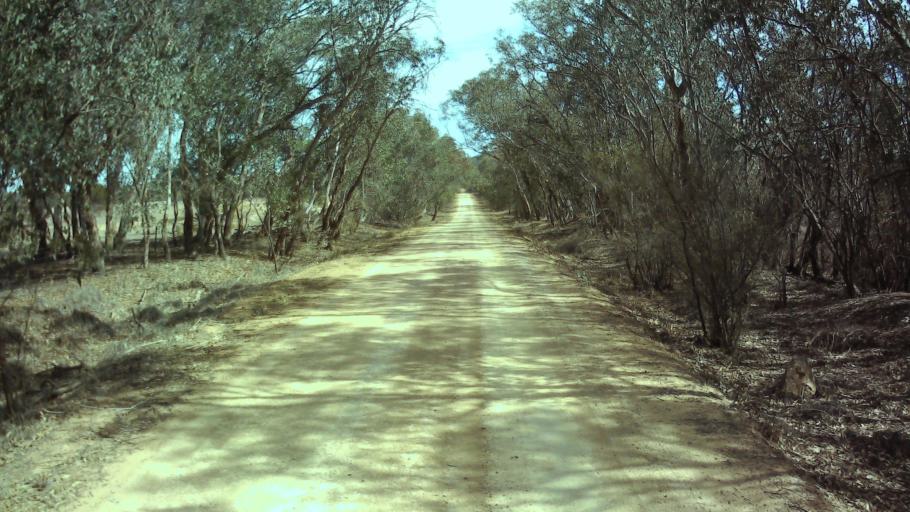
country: AU
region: New South Wales
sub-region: Weddin
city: Grenfell
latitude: -33.8758
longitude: 148.1490
